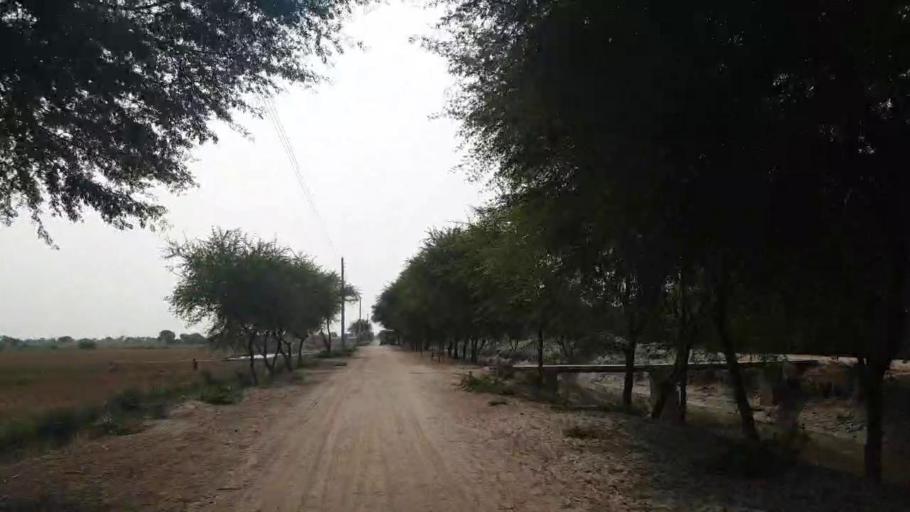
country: PK
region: Sindh
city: Badin
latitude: 24.6172
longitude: 68.7231
